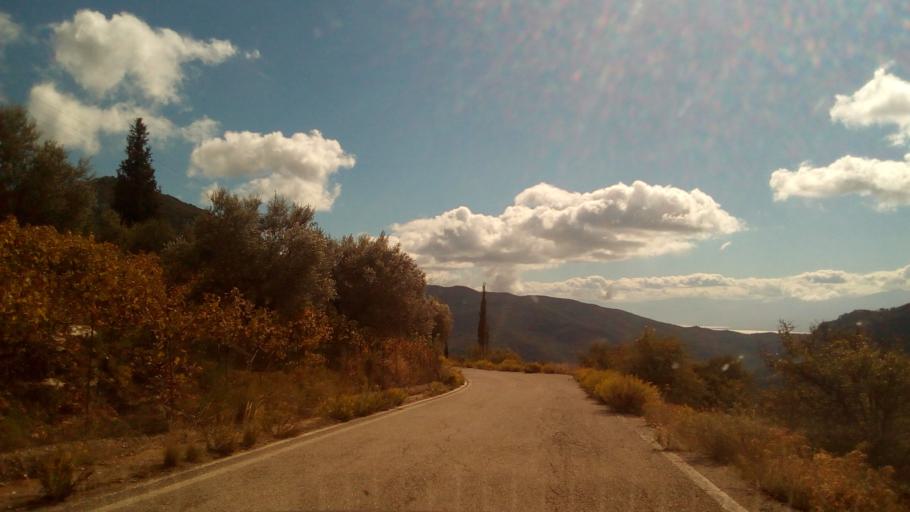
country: GR
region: West Greece
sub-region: Nomos Aitolias kai Akarnanias
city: Nafpaktos
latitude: 38.4833
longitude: 21.8564
